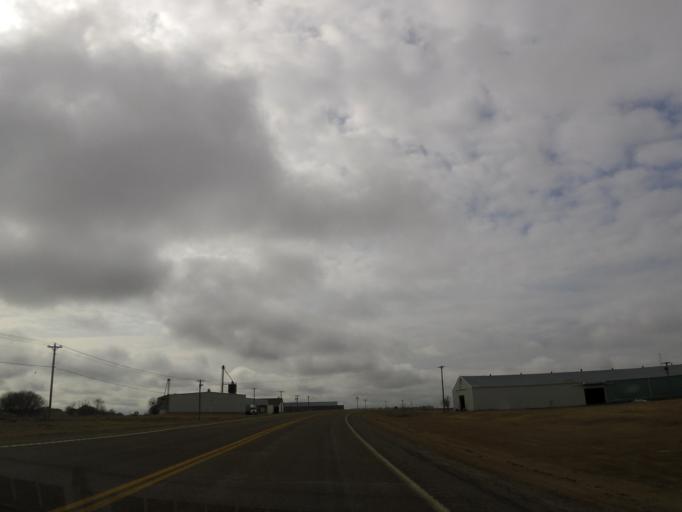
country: US
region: North Dakota
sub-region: Traill County
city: Mayville
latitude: 47.4862
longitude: -97.3227
